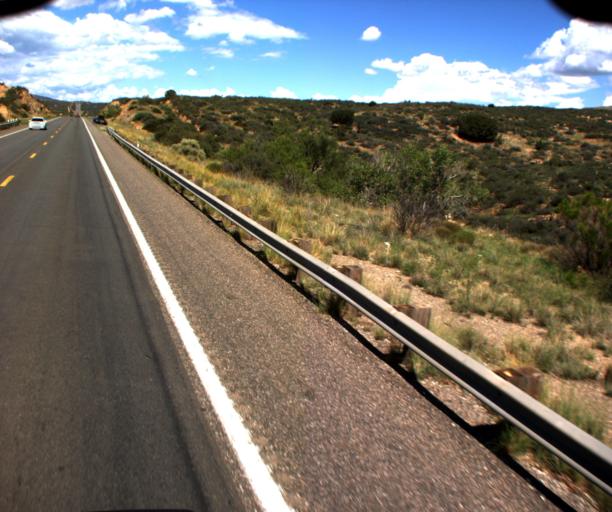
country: US
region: Arizona
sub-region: Yavapai County
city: Dewey-Humboldt
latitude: 34.5277
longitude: -112.0976
